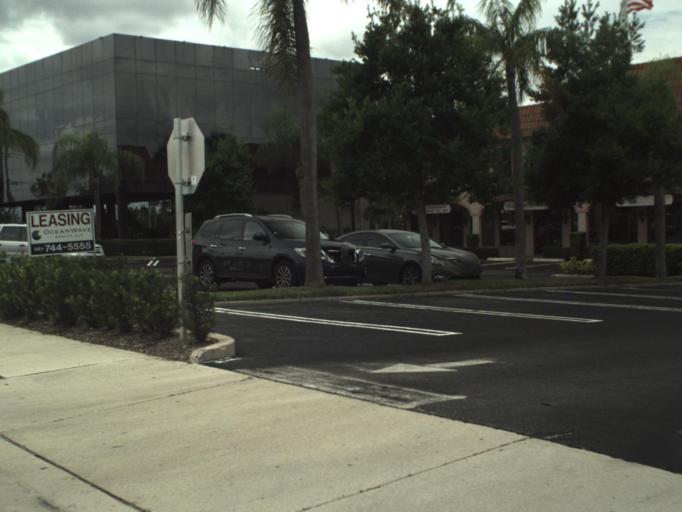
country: US
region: Florida
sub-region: Palm Beach County
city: Jupiter
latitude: 26.9569
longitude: -80.0850
